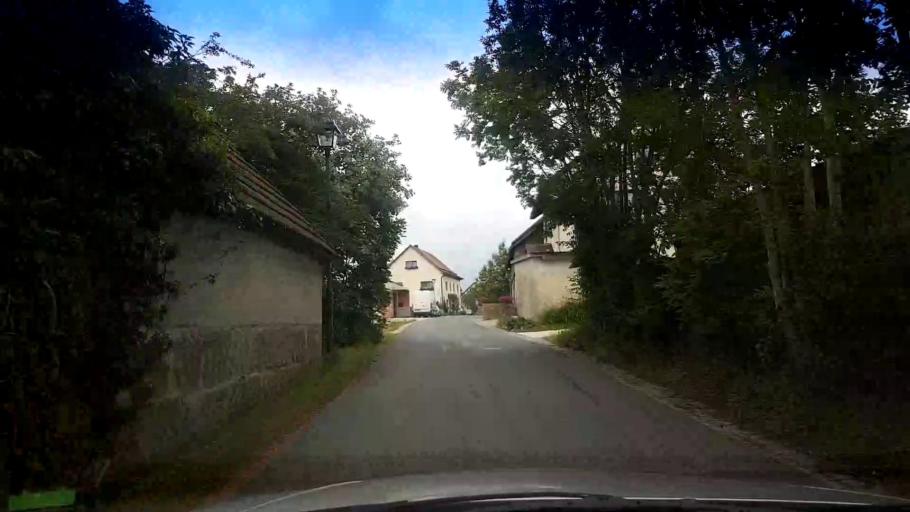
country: DE
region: Bavaria
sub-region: Upper Franconia
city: Poxdorf
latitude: 49.8925
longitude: 11.0842
